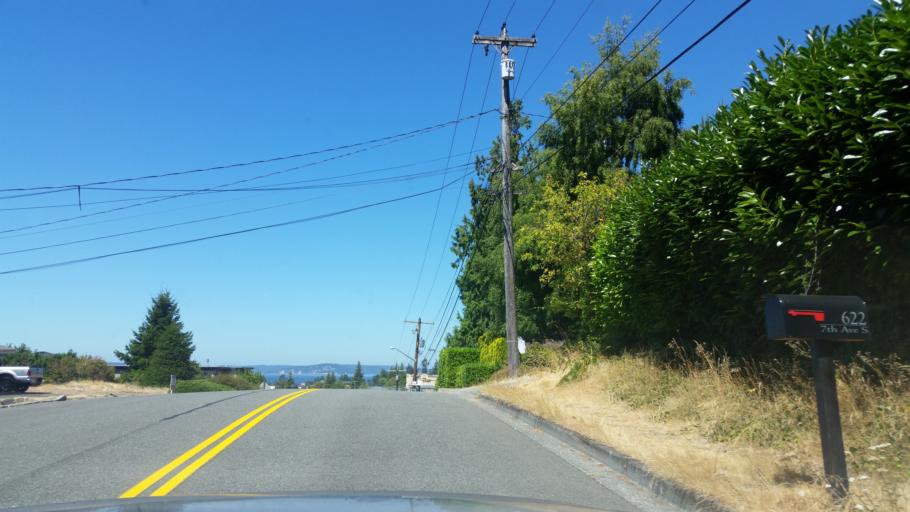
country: US
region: Washington
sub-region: Snohomish County
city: Edmonds
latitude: 47.8059
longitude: -122.3722
